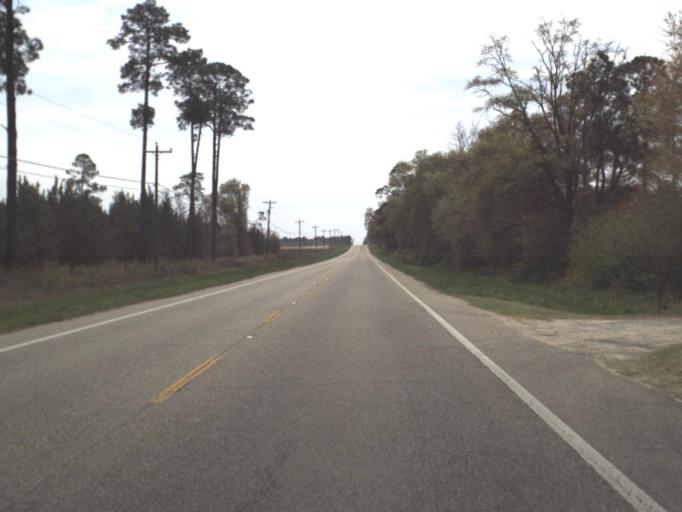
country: US
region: Florida
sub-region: Jackson County
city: Graceville
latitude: 30.9159
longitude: -85.5209
